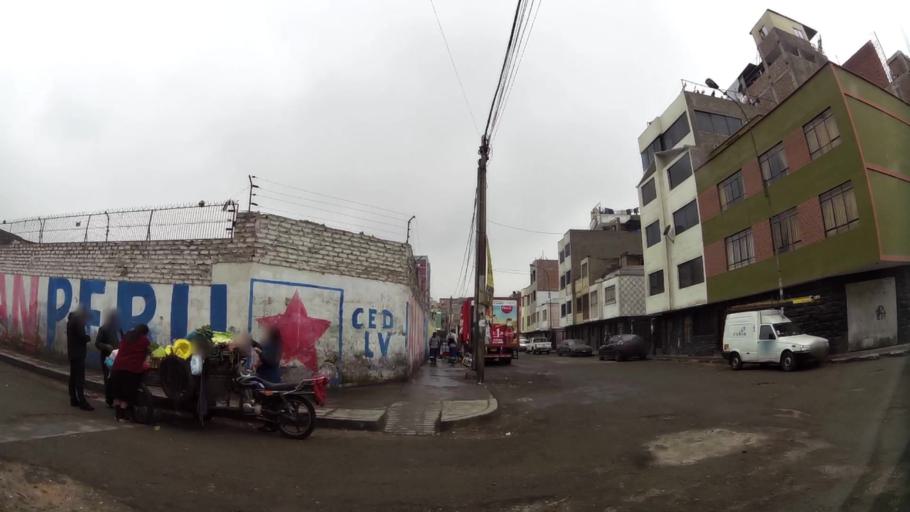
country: PE
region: Lima
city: Lima
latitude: -12.0603
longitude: -77.0246
